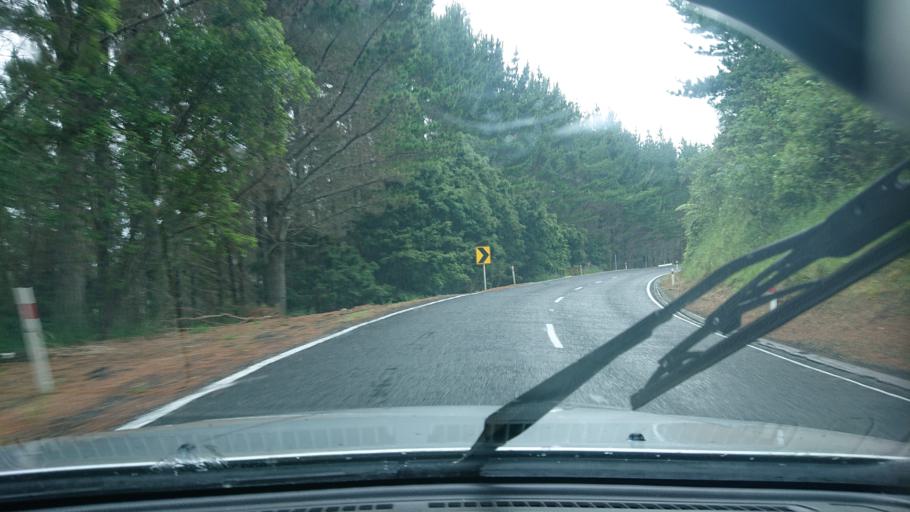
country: NZ
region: Auckland
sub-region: Auckland
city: Wellsford
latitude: -36.3599
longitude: 174.4673
